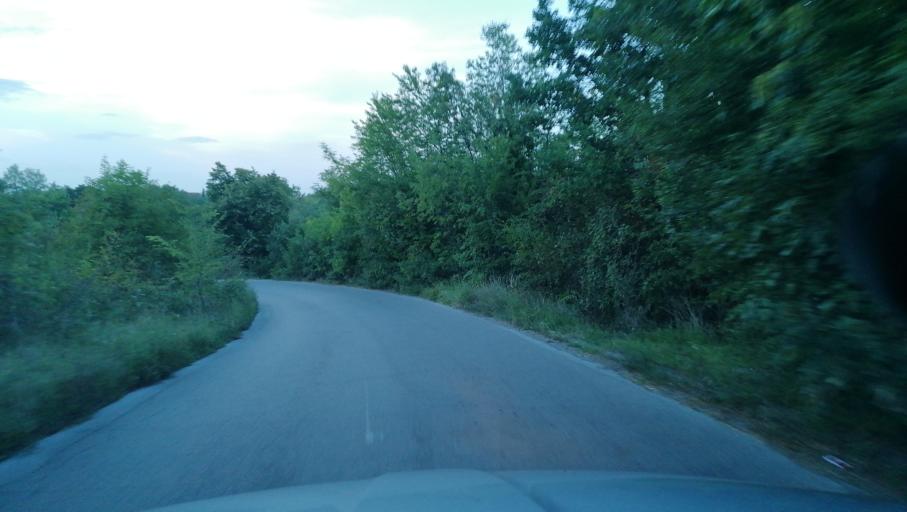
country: RS
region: Central Serbia
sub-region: Kolubarski Okrug
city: Valjevo
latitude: 44.2490
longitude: 19.8730
